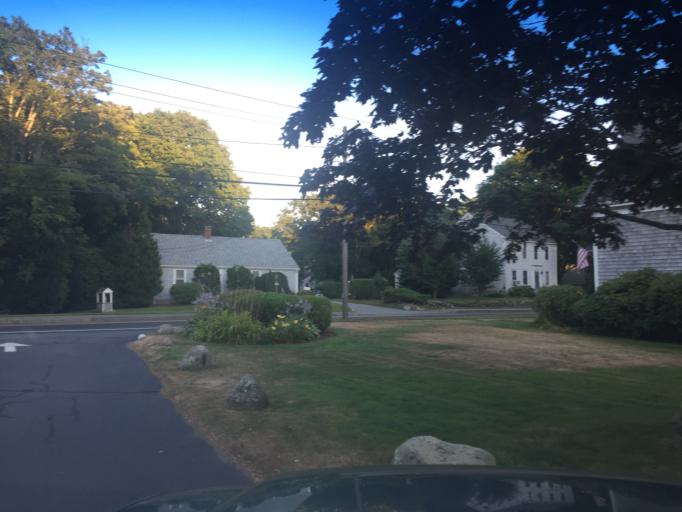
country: US
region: Massachusetts
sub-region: Barnstable County
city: Falmouth
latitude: 41.5624
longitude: -70.6193
